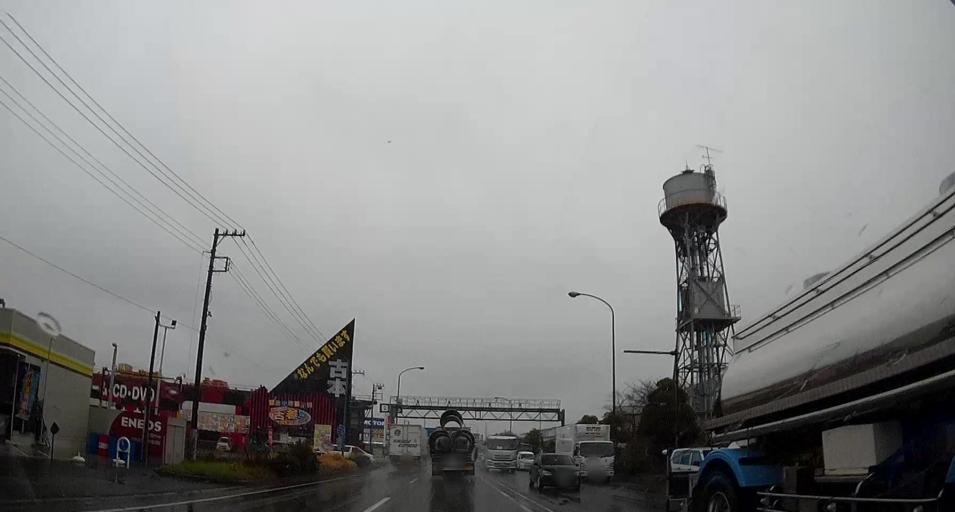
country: JP
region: Chiba
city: Chiba
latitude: 35.5618
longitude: 140.1281
